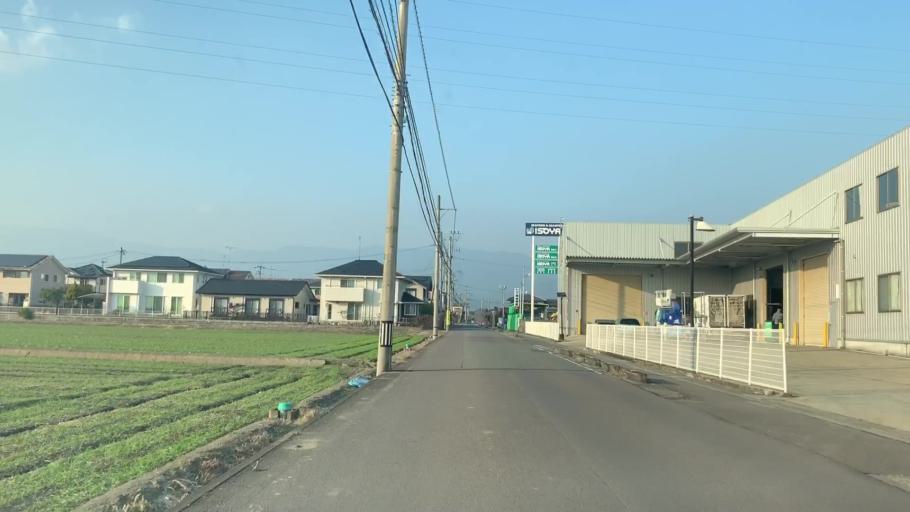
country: JP
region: Saga Prefecture
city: Saga-shi
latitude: 33.2678
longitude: 130.2302
